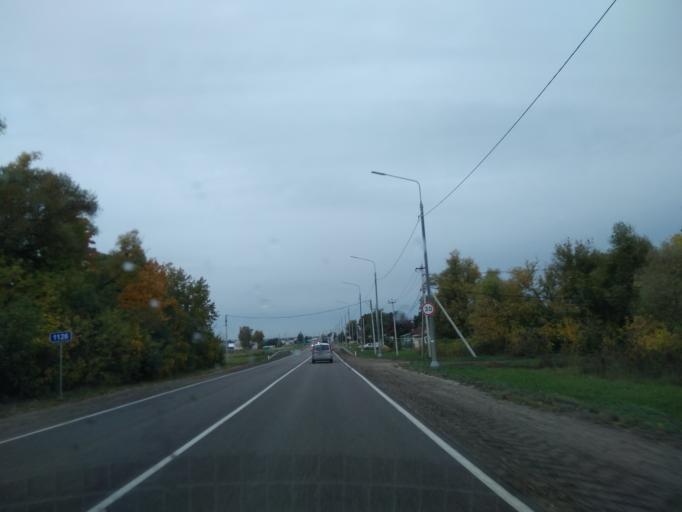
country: RU
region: Lipetsk
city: Zadonsk
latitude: 52.4304
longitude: 38.8342
